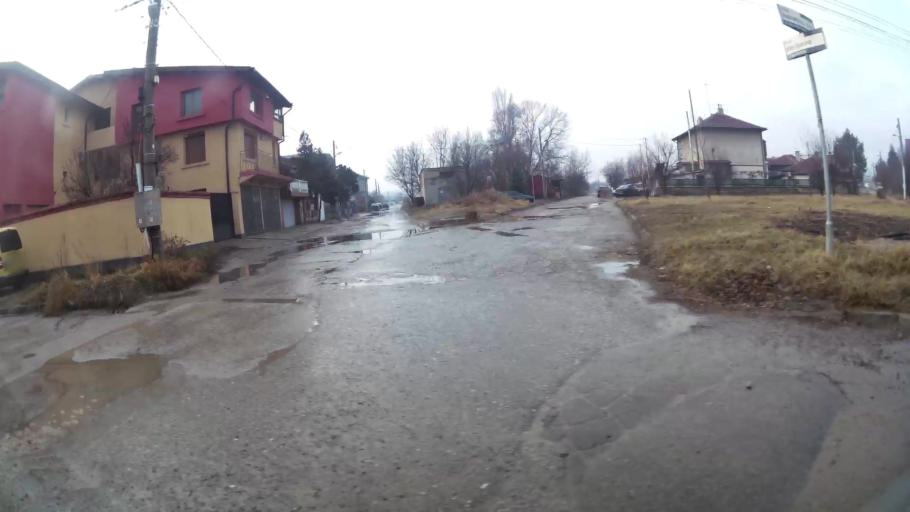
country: BG
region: Sofia-Capital
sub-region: Stolichna Obshtina
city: Sofia
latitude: 42.7366
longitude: 23.3395
